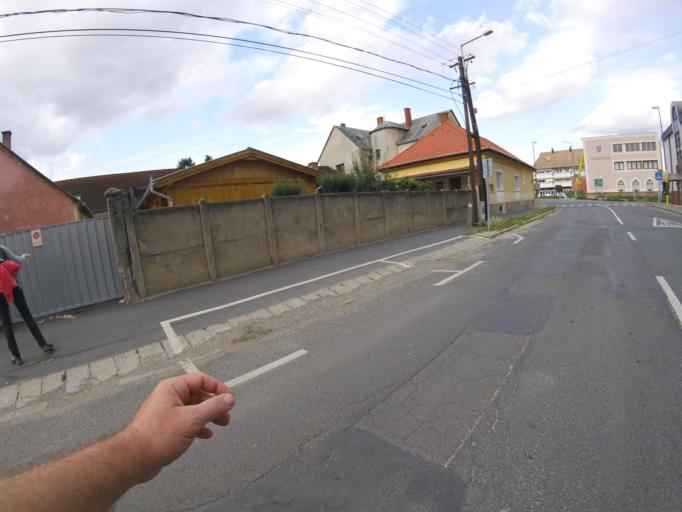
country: HU
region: Vas
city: Csepreg
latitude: 47.4010
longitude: 16.7068
